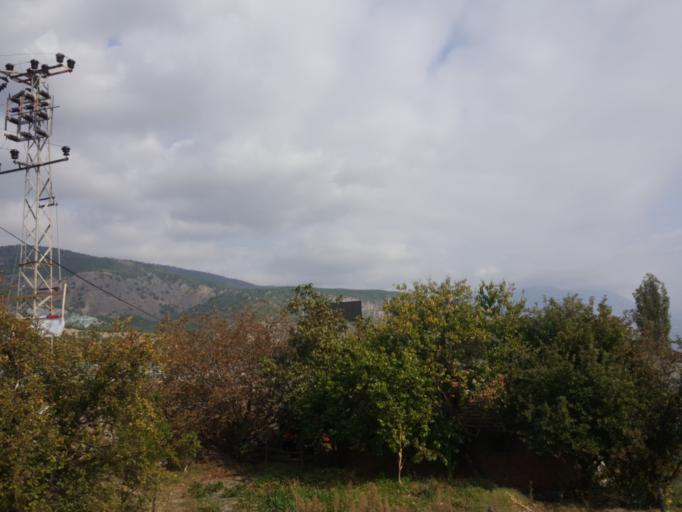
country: TR
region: Corum
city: Hacihamza
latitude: 41.0956
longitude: 34.3539
